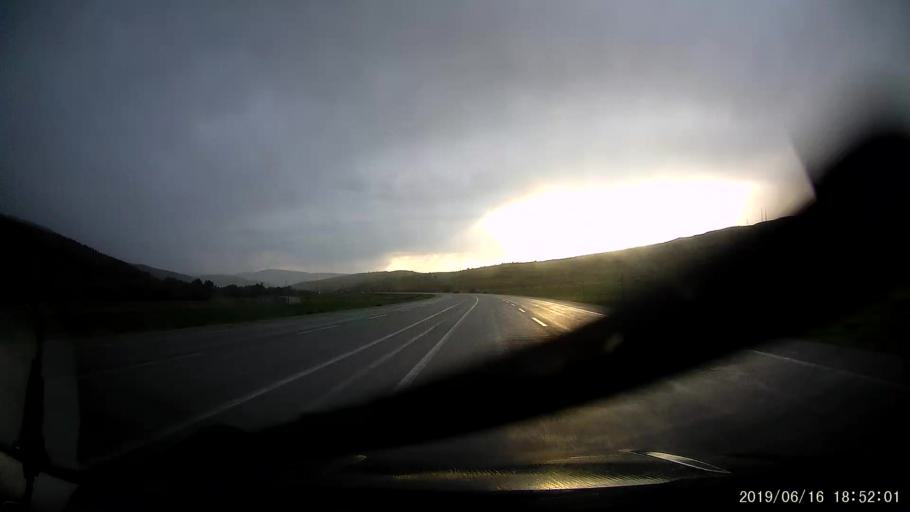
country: TR
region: Erzincan
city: Catalcam
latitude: 39.9025
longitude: 38.9122
